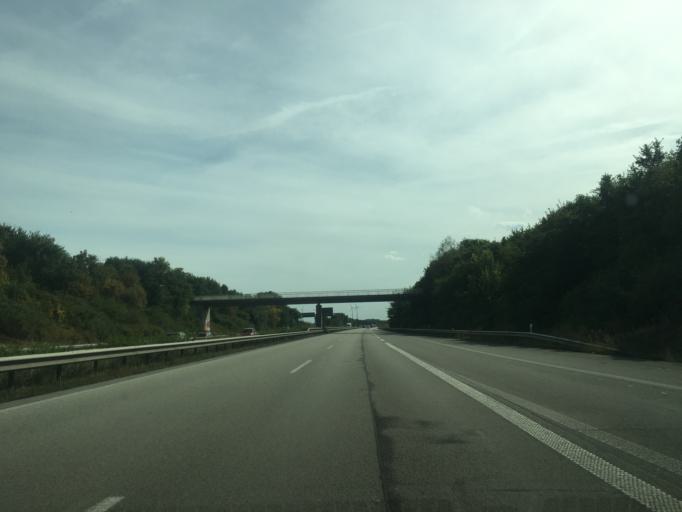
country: DE
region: Rheinland-Pfalz
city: Kleinniedesheim
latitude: 49.6206
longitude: 8.2934
